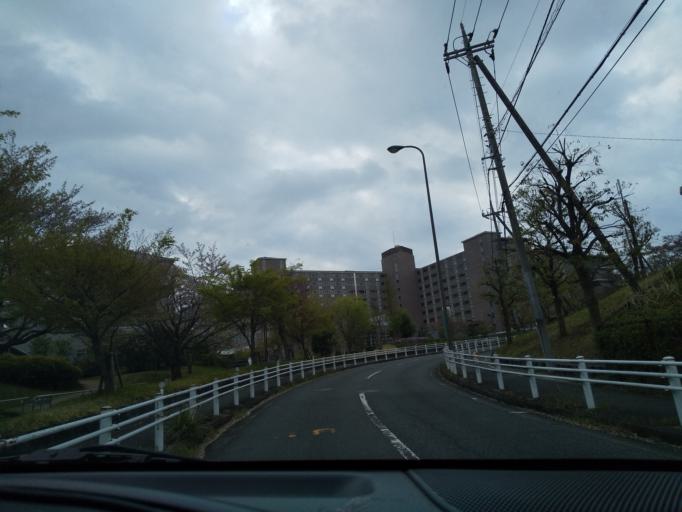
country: JP
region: Tokyo
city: Hino
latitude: 35.6050
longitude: 139.3807
